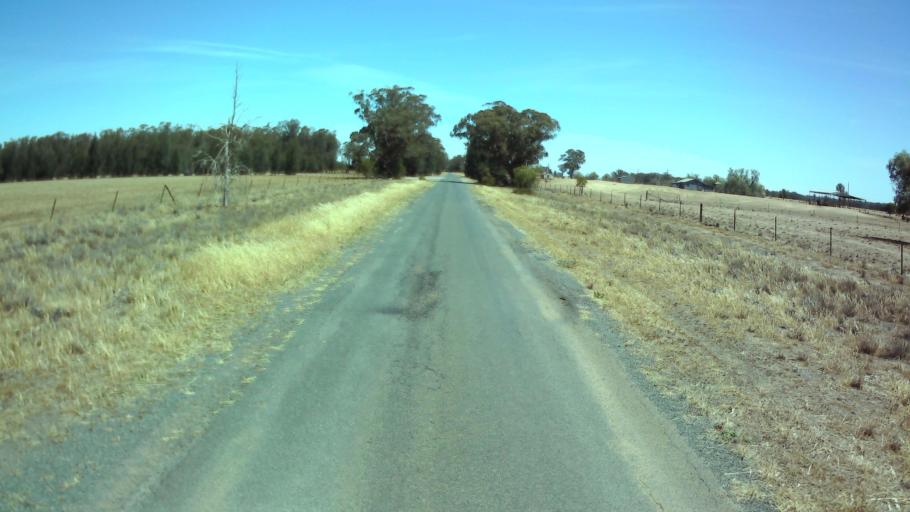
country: AU
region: New South Wales
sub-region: Weddin
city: Grenfell
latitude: -33.9018
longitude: 147.6862
